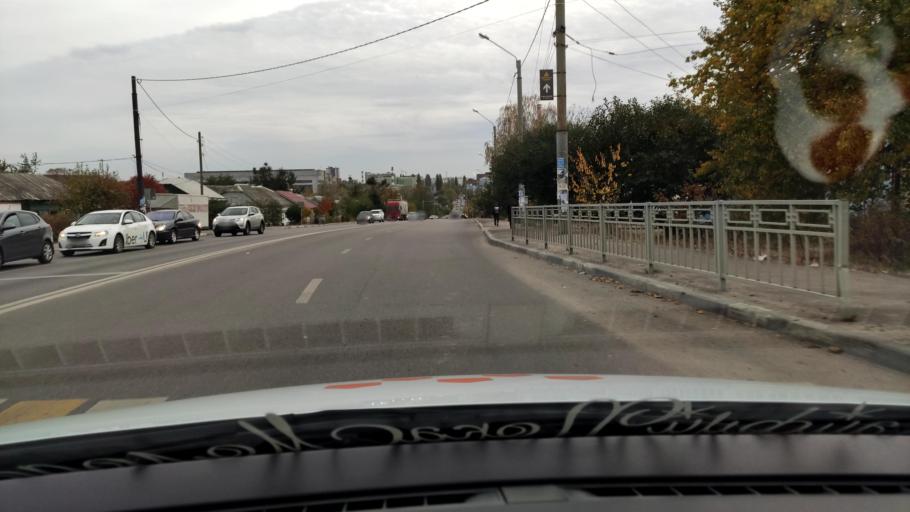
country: RU
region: Voronezj
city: Voronezh
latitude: 51.6969
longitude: 39.1569
